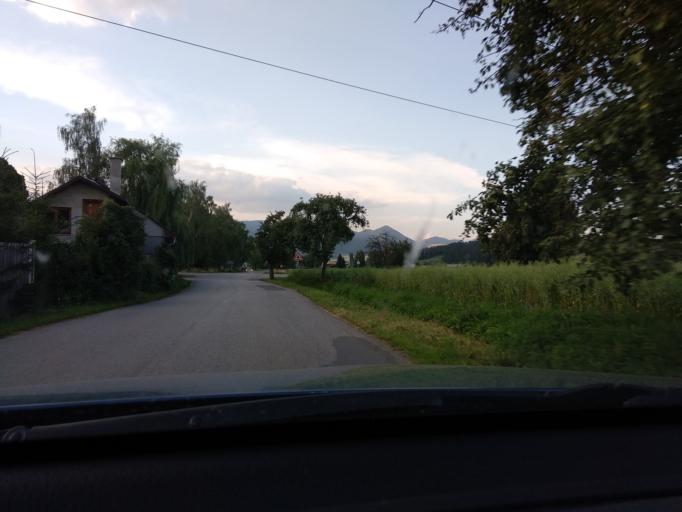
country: SK
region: Zilinsky
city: Ruzomberok
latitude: 49.0612
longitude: 19.3359
